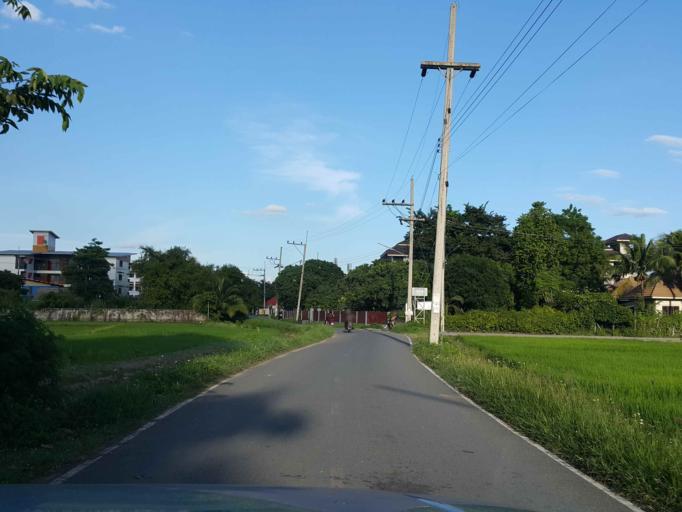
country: TH
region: Chiang Mai
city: San Sai
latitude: 18.8961
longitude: 98.9972
